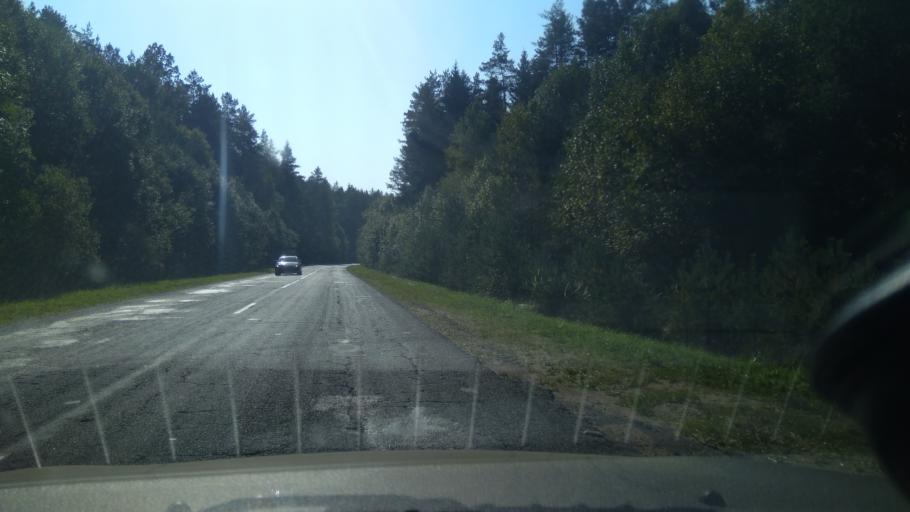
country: BY
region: Minsk
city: Rakaw
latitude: 53.9986
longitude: 27.0453
